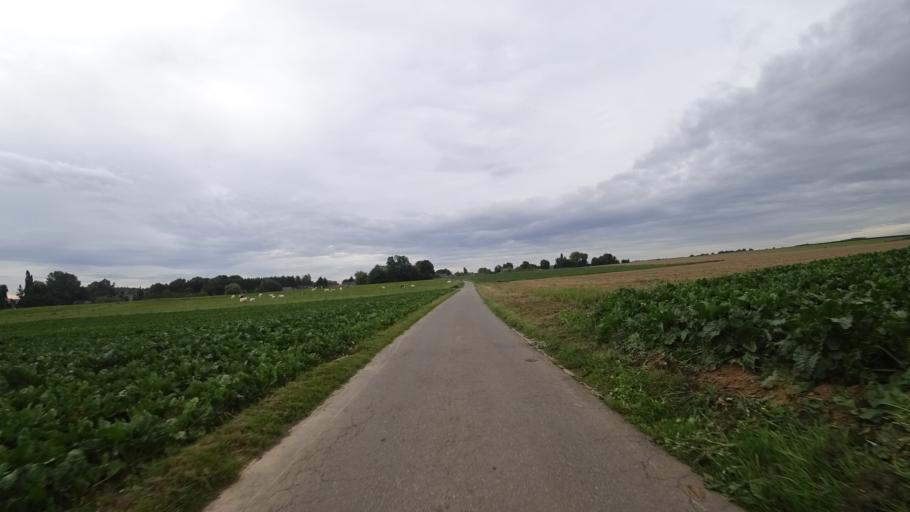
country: BE
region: Wallonia
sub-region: Province du Brabant Wallon
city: Perwez
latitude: 50.5735
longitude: 4.7671
